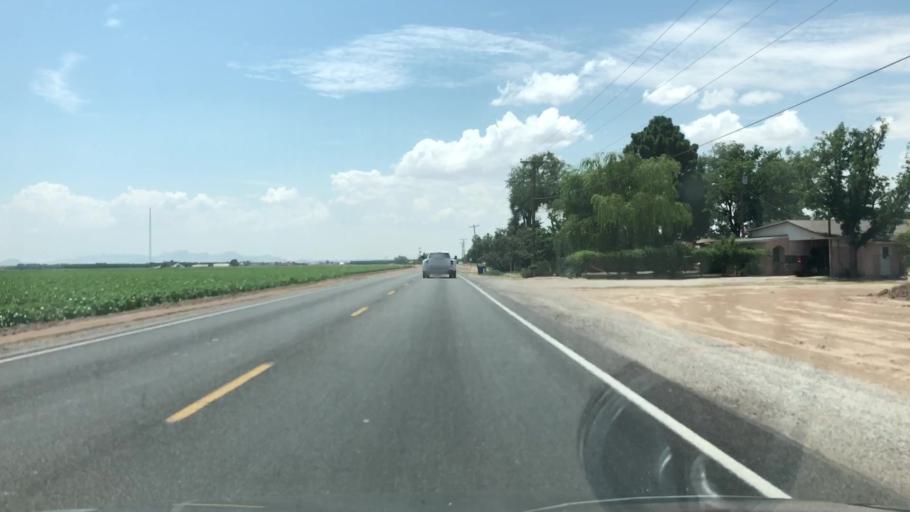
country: US
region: New Mexico
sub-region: Dona Ana County
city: La Union
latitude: 31.9780
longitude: -106.6515
